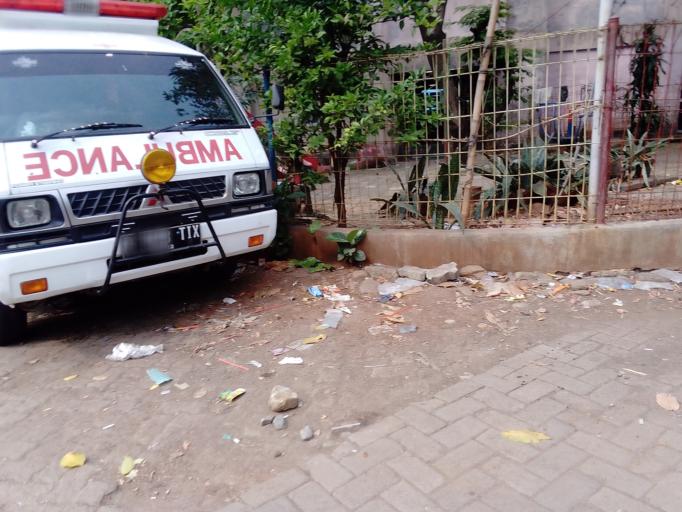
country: ID
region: Jakarta Raya
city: Jakarta
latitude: -6.2007
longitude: 106.8079
